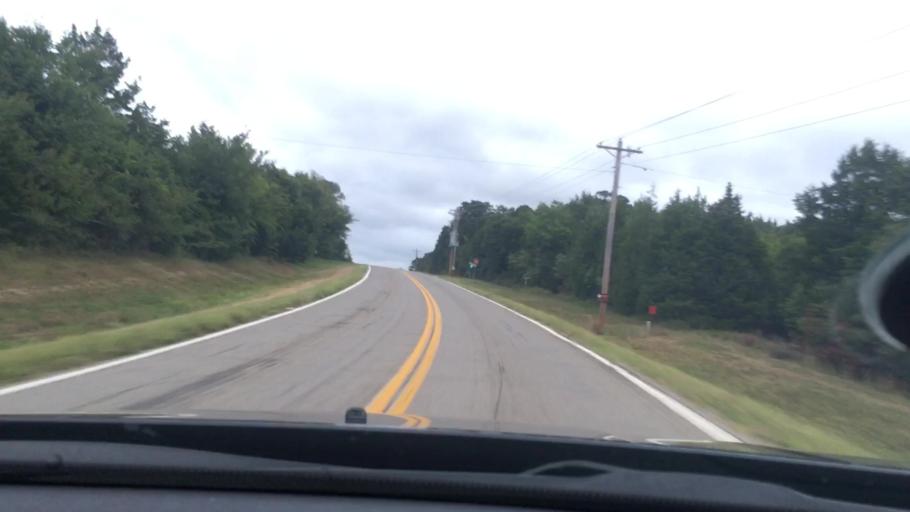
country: US
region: Oklahoma
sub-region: Sequoyah County
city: Vian
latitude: 35.6029
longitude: -95.0038
